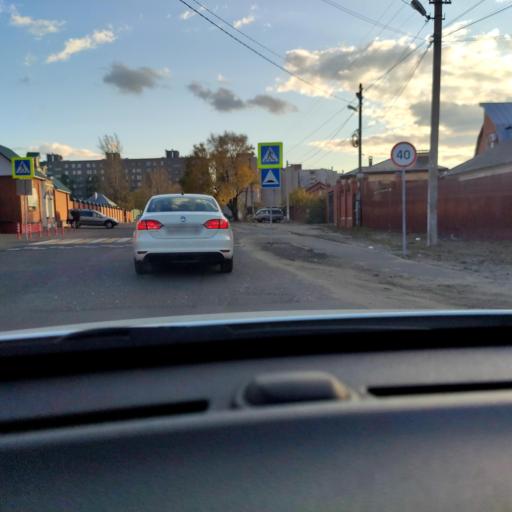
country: RU
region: Voronezj
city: Voronezh
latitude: 51.7005
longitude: 39.2685
